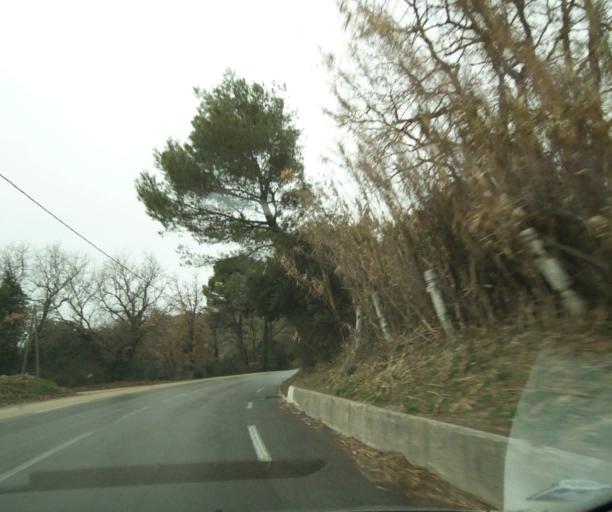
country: FR
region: Provence-Alpes-Cote d'Azur
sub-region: Departement des Bouches-du-Rhone
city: Rognes
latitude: 43.6612
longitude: 5.3701
